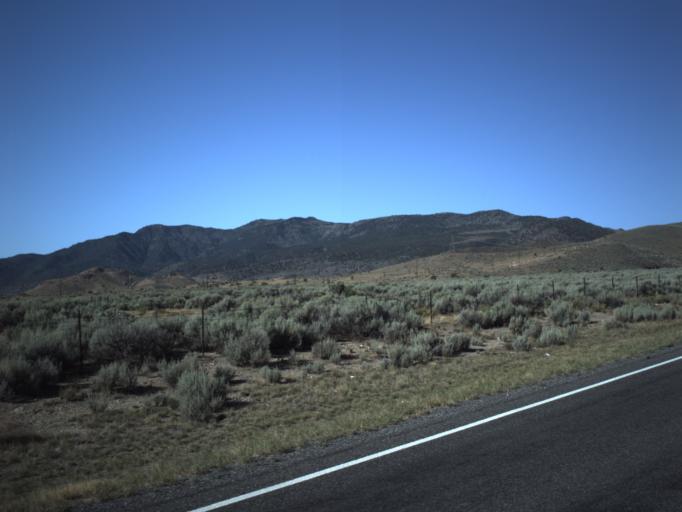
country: US
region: Utah
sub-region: Utah County
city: Genola
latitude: 39.9514
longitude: -111.9946
